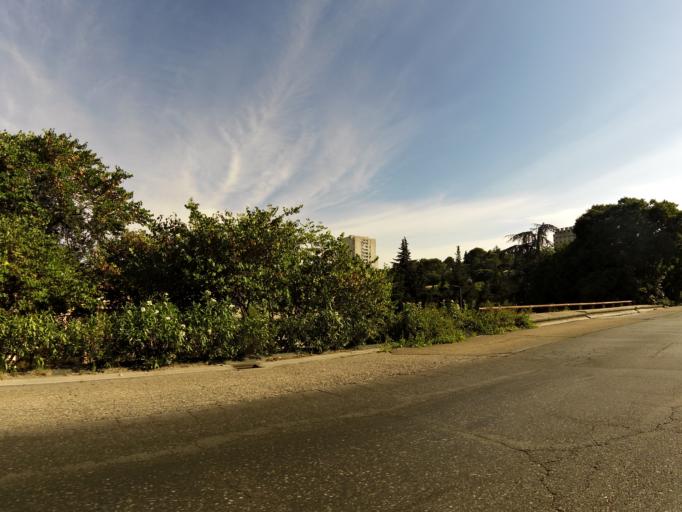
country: FR
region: Languedoc-Roussillon
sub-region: Departement du Gard
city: Nimes
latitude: 43.8311
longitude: 4.3403
